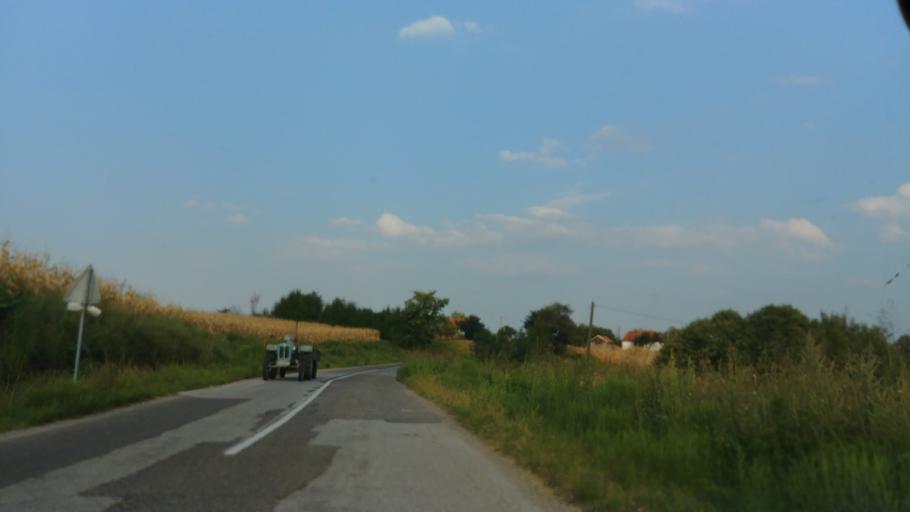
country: BA
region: Republika Srpska
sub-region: Opstina Ugljevik
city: Ugljevik
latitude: 44.7074
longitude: 18.9824
